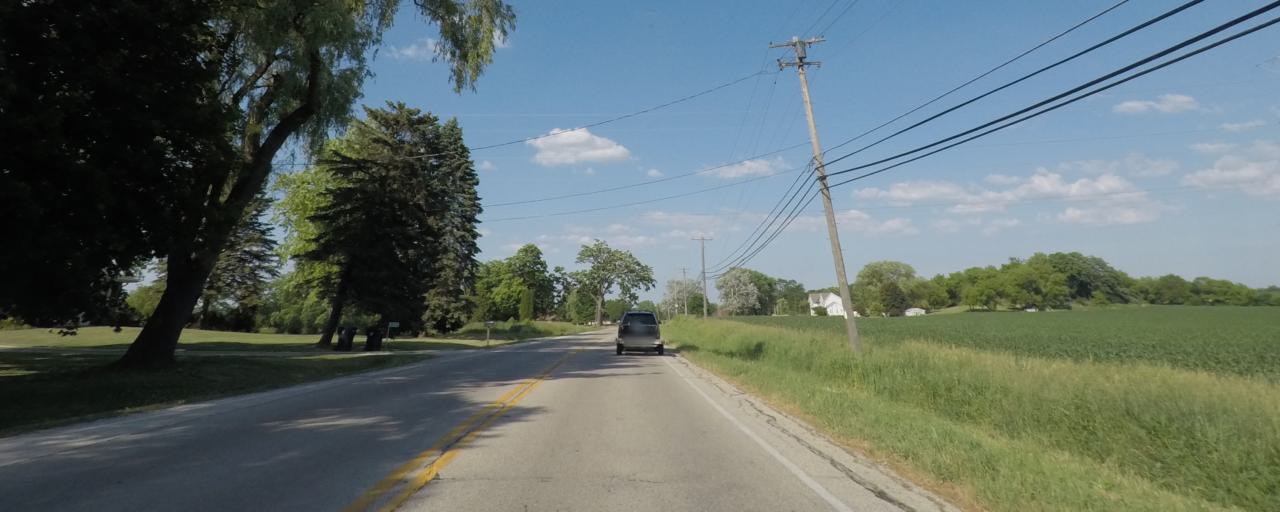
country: US
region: Wisconsin
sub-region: Waukesha County
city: Big Bend
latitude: 42.8705
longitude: -88.2204
